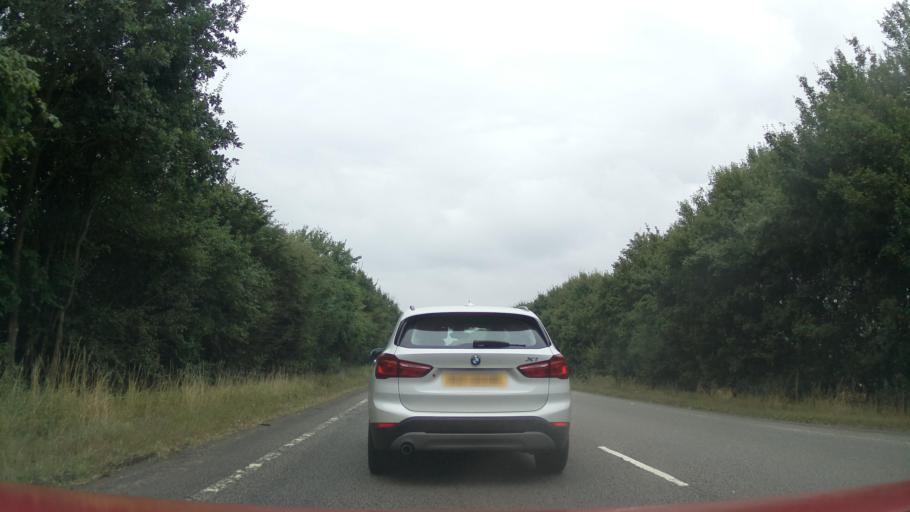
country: GB
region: England
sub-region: Nottinghamshire
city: South Collingham
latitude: 53.0909
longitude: -0.7645
